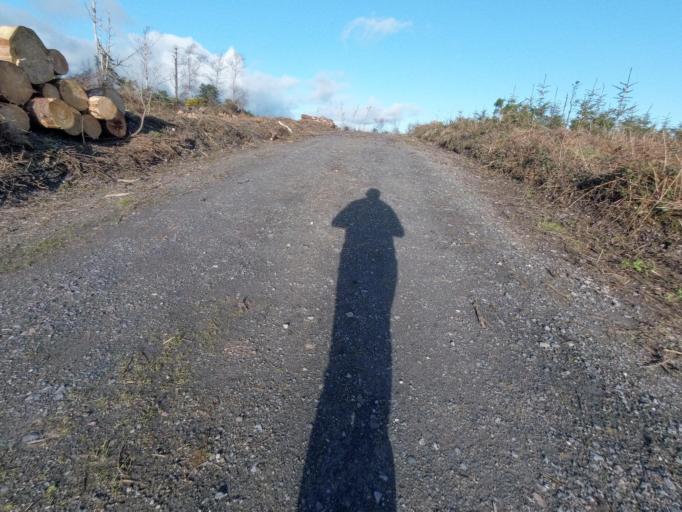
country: IE
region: Munster
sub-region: Waterford
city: Waterford
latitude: 52.2660
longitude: -7.0102
